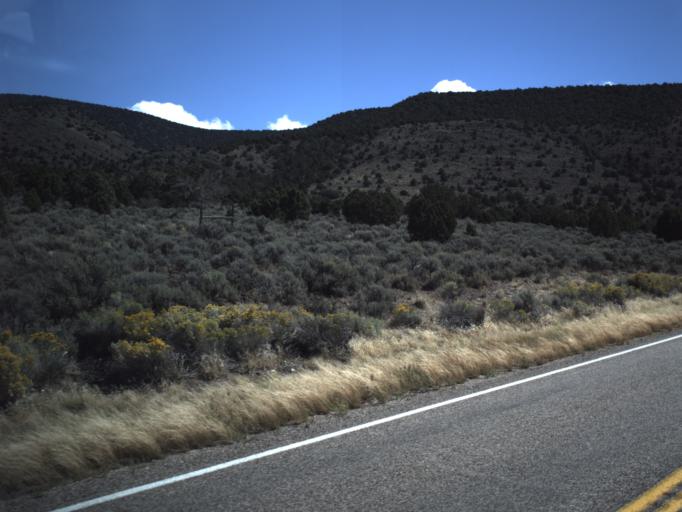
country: US
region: Utah
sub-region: Beaver County
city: Milford
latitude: 38.1250
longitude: -112.9550
